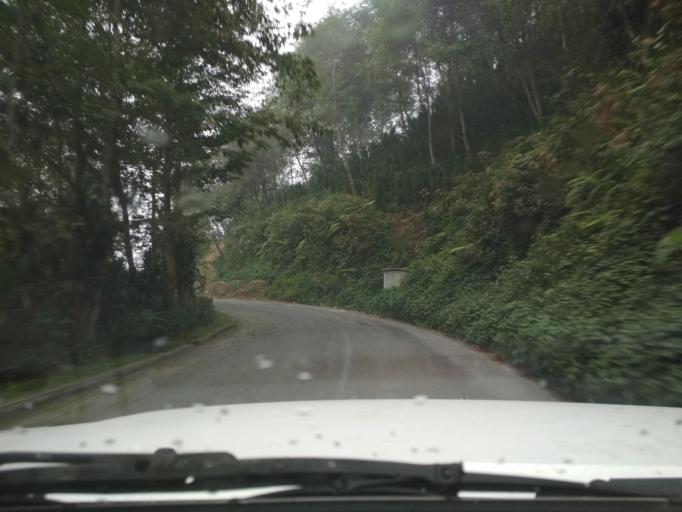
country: MX
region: Veracruz
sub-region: La Perla
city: Metlac Hernandez (Metlac Primero)
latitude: 18.9519
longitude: -97.1680
